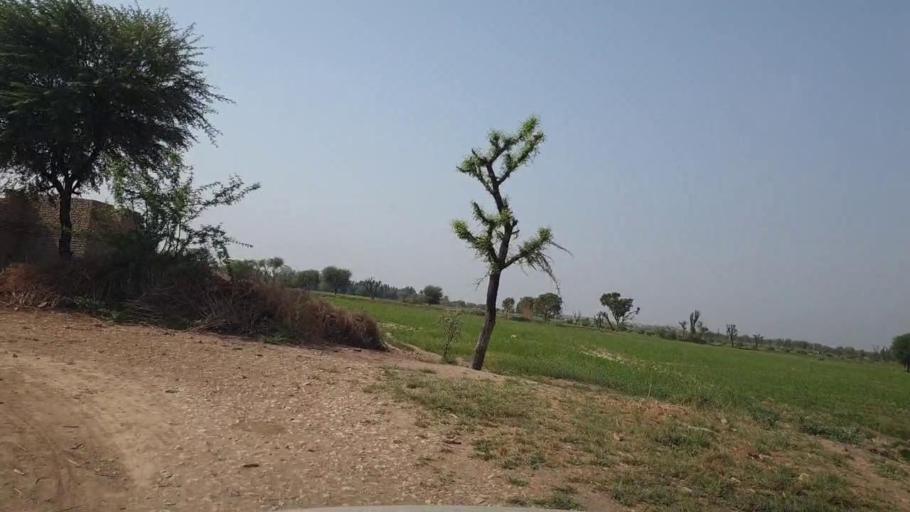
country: PK
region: Sindh
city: Dhoro Naro
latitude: 25.4882
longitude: 69.6088
